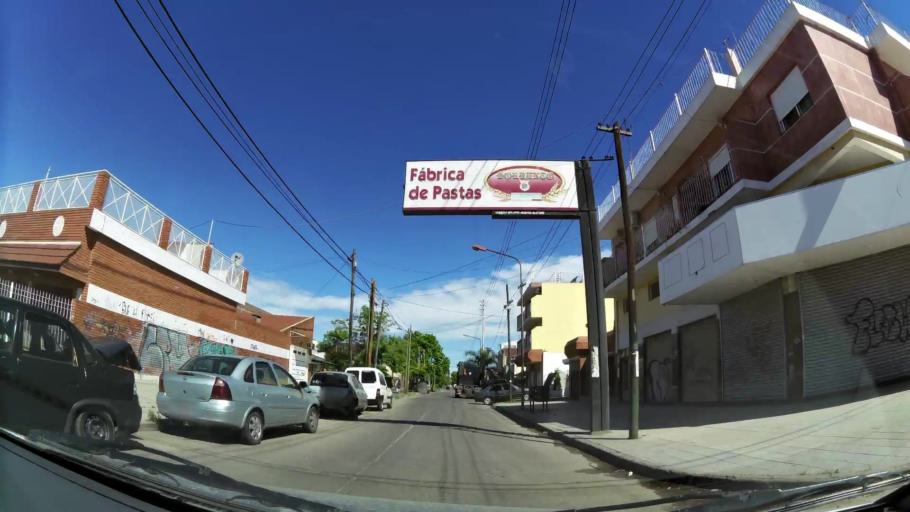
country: AR
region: Buenos Aires
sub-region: Partido de Almirante Brown
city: Adrogue
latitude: -34.7654
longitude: -58.3599
